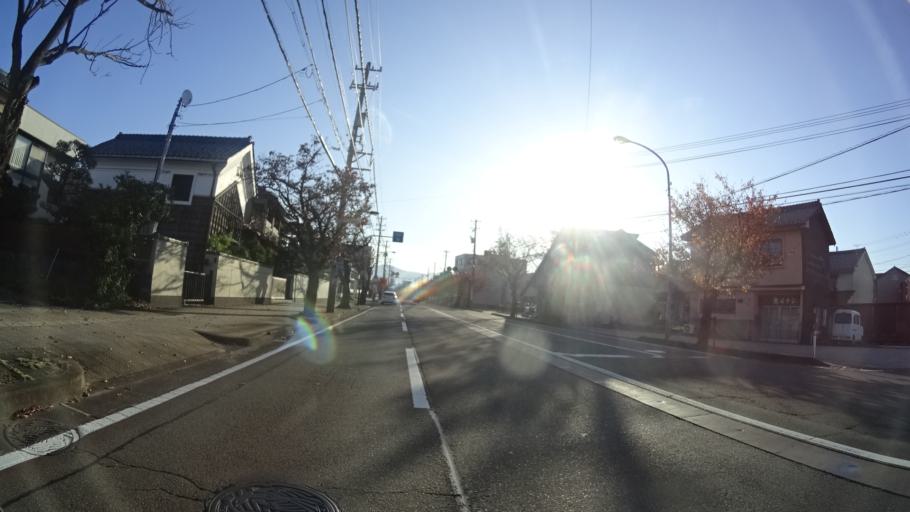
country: JP
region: Fukui
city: Fukui-shi
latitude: 36.0643
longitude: 136.2366
